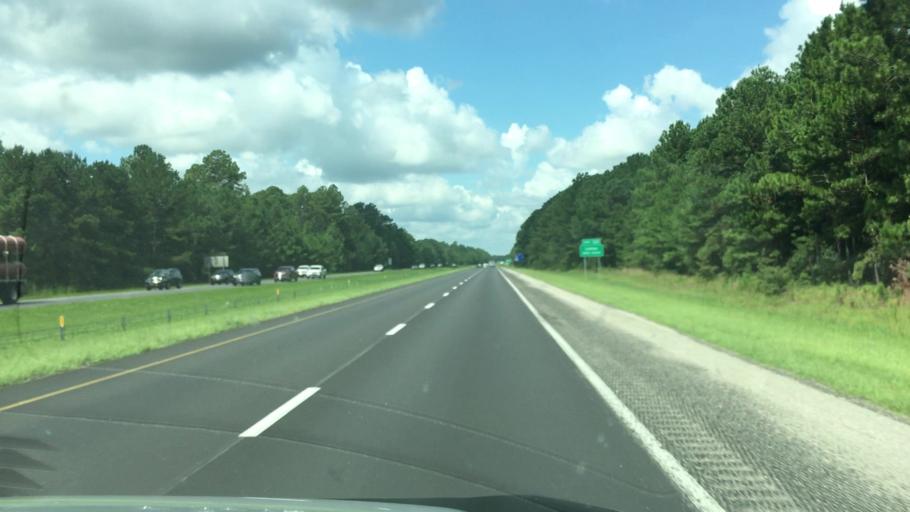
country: US
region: South Carolina
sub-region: Florence County
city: Timmonsville
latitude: 34.2056
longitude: -80.0096
